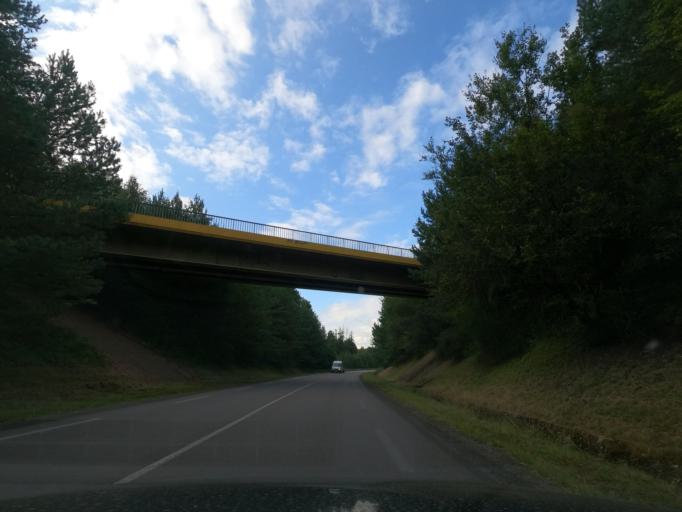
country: FR
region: Haute-Normandie
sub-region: Departement de l'Eure
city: Bernay
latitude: 49.0791
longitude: 0.5740
